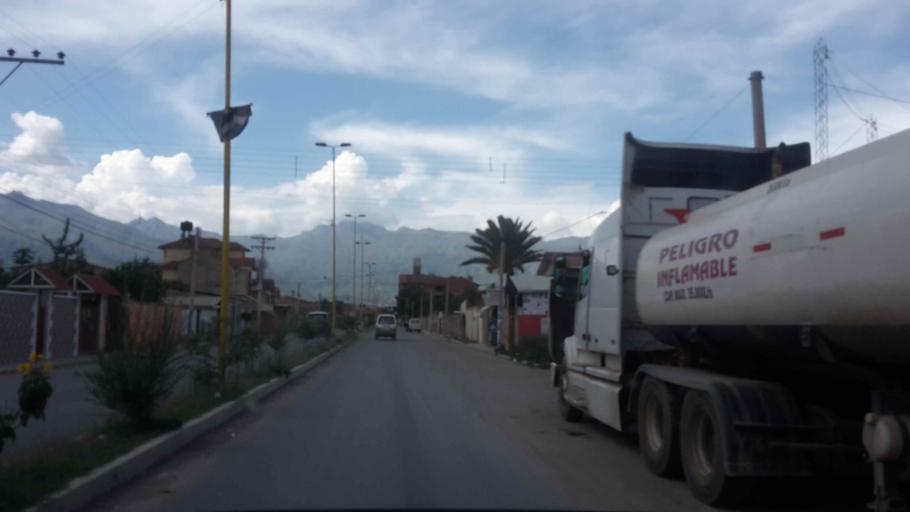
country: BO
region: Cochabamba
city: Sipe Sipe
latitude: -17.4067
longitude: -66.2863
